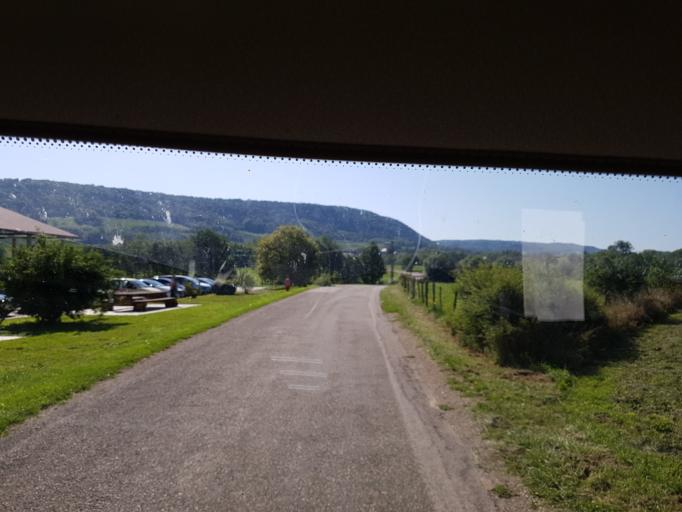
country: FR
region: Franche-Comte
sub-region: Departement du Jura
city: Perrigny
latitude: 46.7259
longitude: 5.5911
